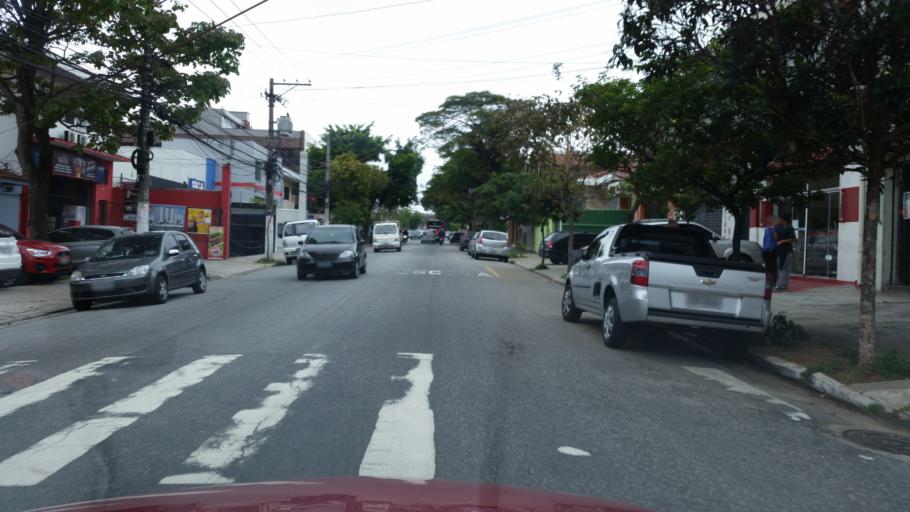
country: BR
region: Sao Paulo
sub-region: Diadema
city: Diadema
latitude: -23.6390
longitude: -46.6698
